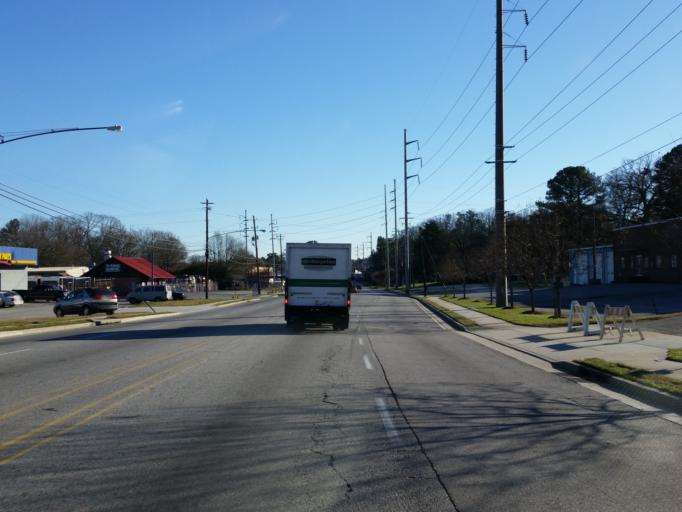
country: US
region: Georgia
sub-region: Cobb County
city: Vinings
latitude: 33.8123
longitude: -84.4392
